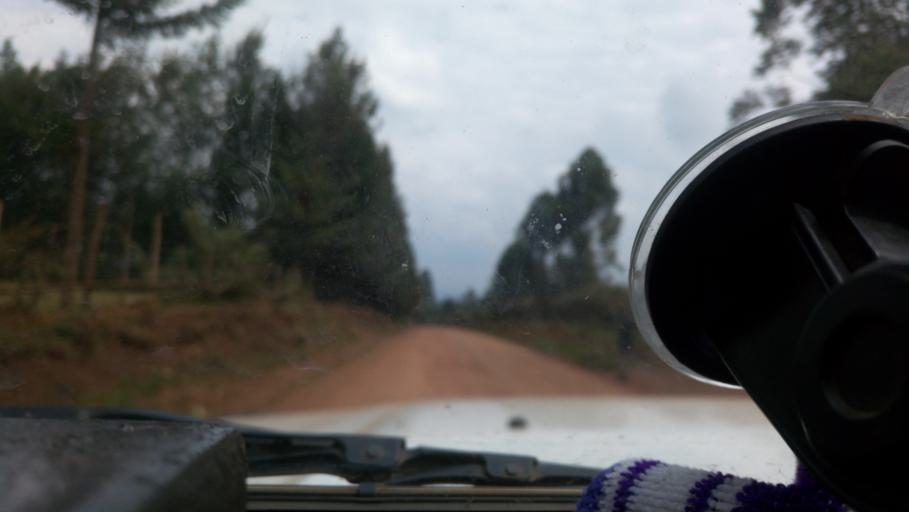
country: KE
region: Kericho
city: Litein
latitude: -0.5995
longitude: 35.1673
